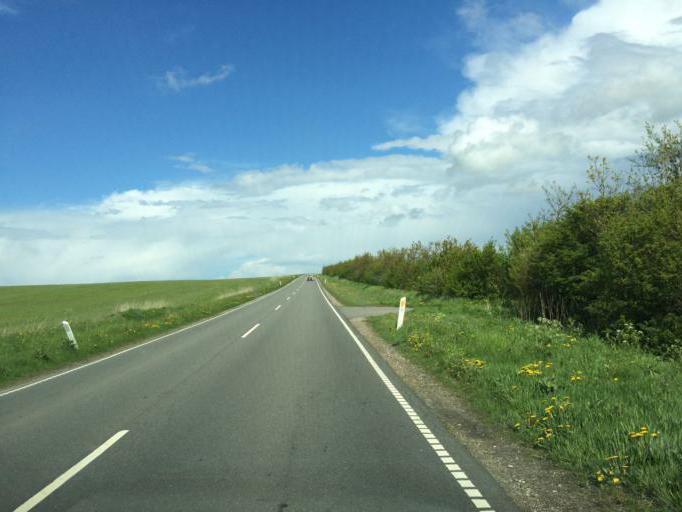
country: DK
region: North Denmark
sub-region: Vesthimmerland Kommune
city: Farso
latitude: 56.8093
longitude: 9.3525
